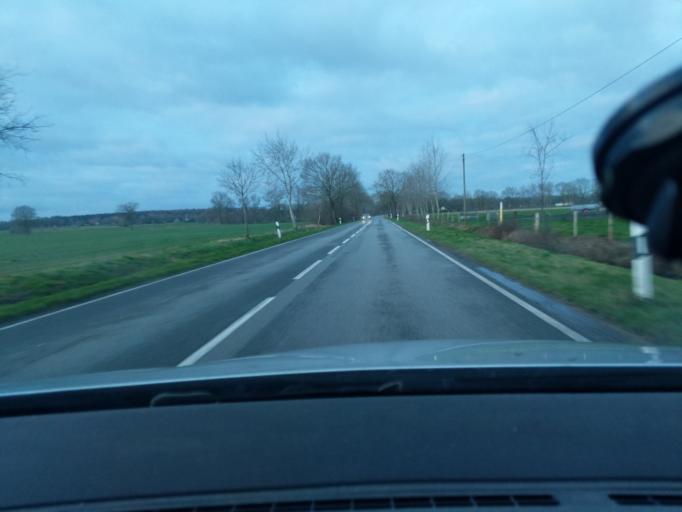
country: DE
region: Lower Saxony
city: Lintig
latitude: 53.6123
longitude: 8.9106
